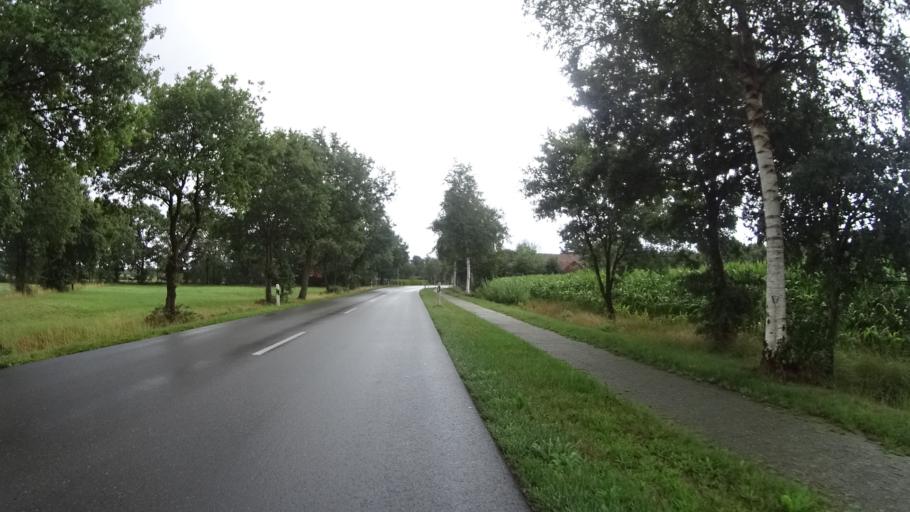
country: DE
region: Lower Saxony
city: Schwerinsdorf
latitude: 53.3435
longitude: 7.7485
